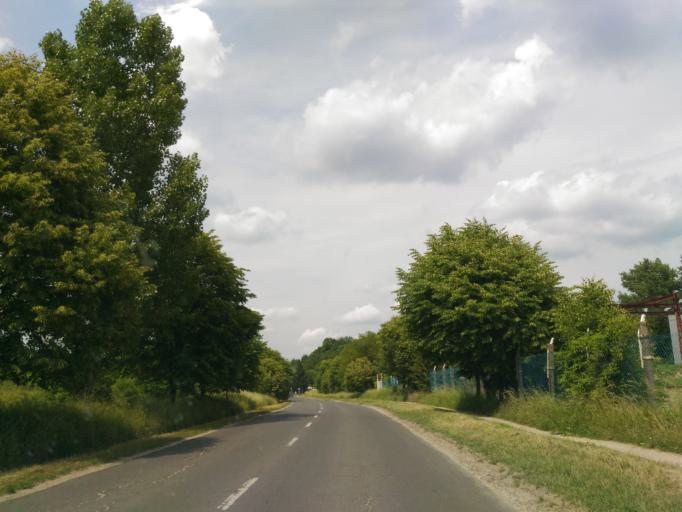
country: HU
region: Baranya
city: Komlo
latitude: 46.1995
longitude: 18.2521
